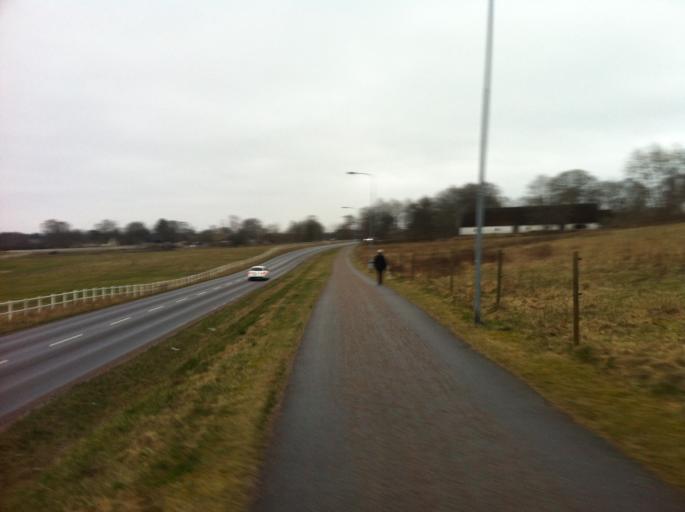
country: SE
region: Skane
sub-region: Hoors Kommun
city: Satofta
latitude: 55.9127
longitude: 13.5498
